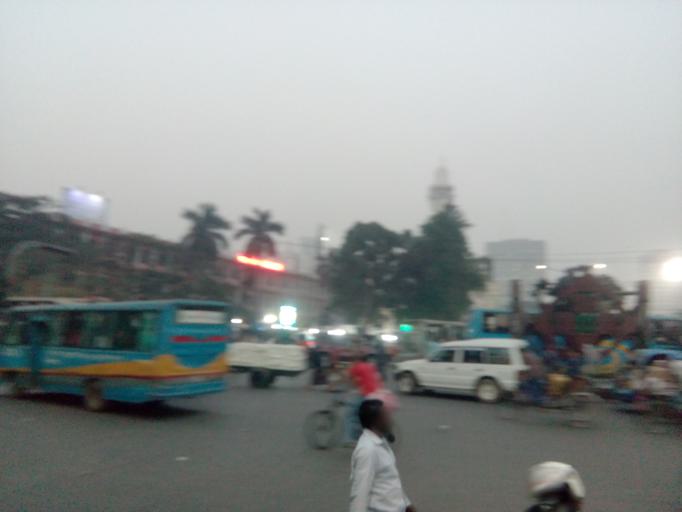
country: BD
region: Dhaka
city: Paltan
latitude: 23.7277
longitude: 90.4103
